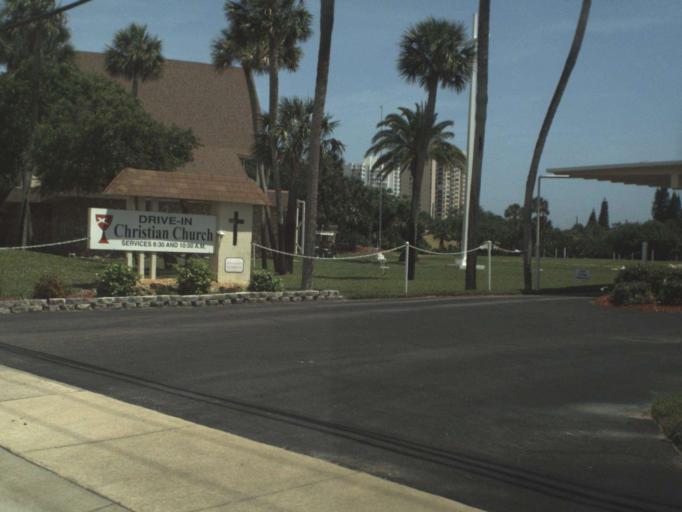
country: US
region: Florida
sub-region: Volusia County
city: Daytona Beach Shores
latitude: 29.1610
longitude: -80.9779
